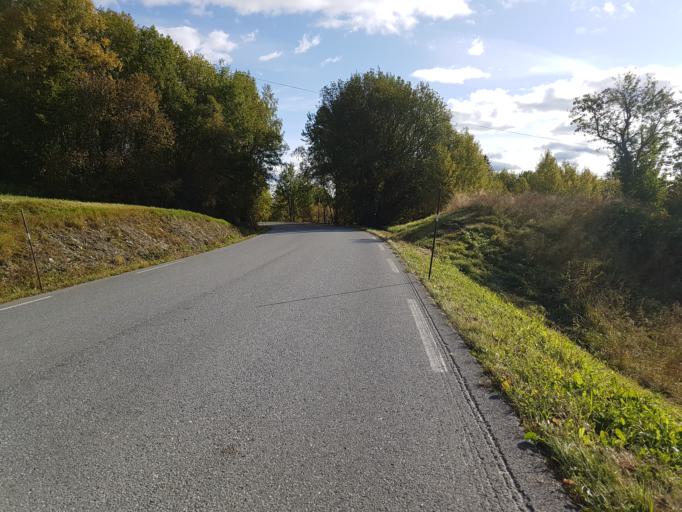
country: NO
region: Sor-Trondelag
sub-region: Malvik
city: Malvik
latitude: 63.3844
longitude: 10.5861
